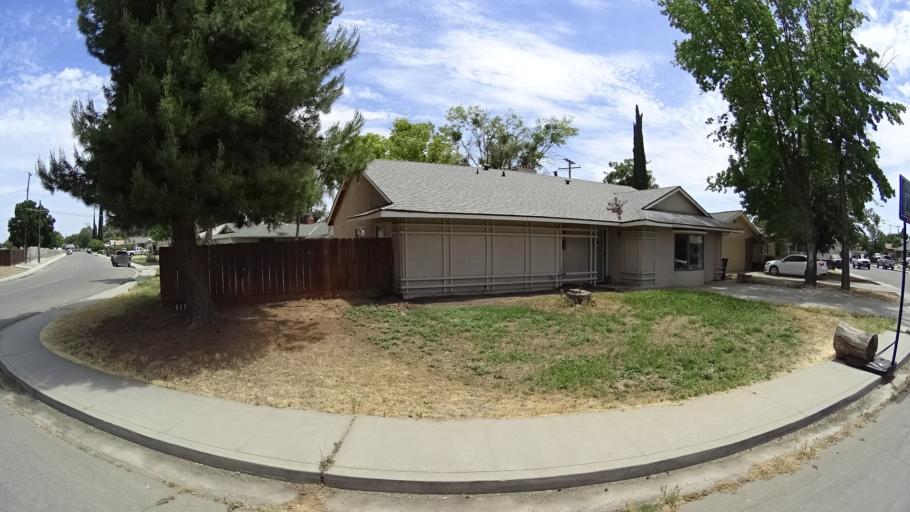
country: US
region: California
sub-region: Kings County
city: Armona
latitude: 36.3105
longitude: -119.7121
